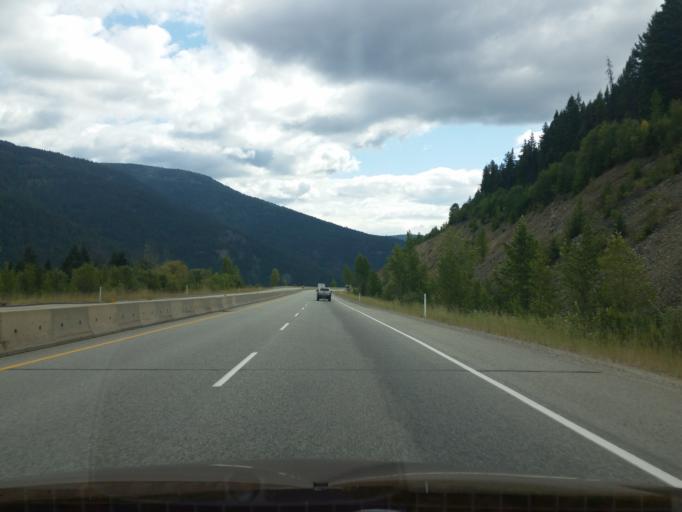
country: CA
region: British Columbia
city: Peachland
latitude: 49.8640
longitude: -119.8669
